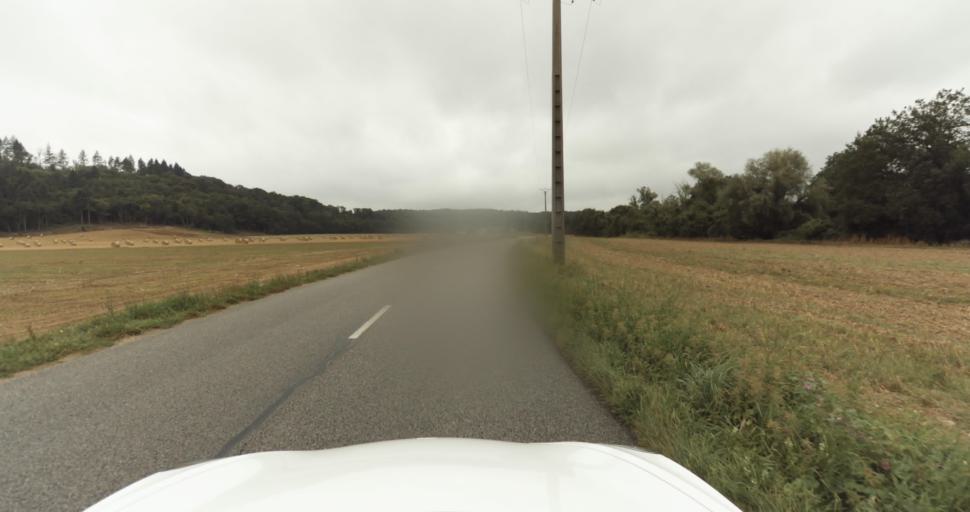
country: FR
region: Haute-Normandie
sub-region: Departement de l'Eure
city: Normanville
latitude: 49.0797
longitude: 1.1435
